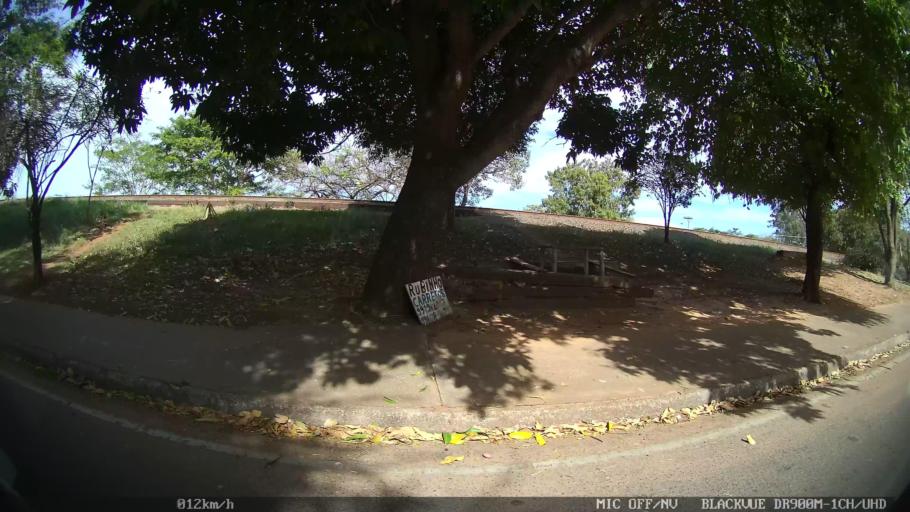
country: BR
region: Sao Paulo
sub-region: Catanduva
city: Catanduva
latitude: -21.1389
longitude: -48.9604
